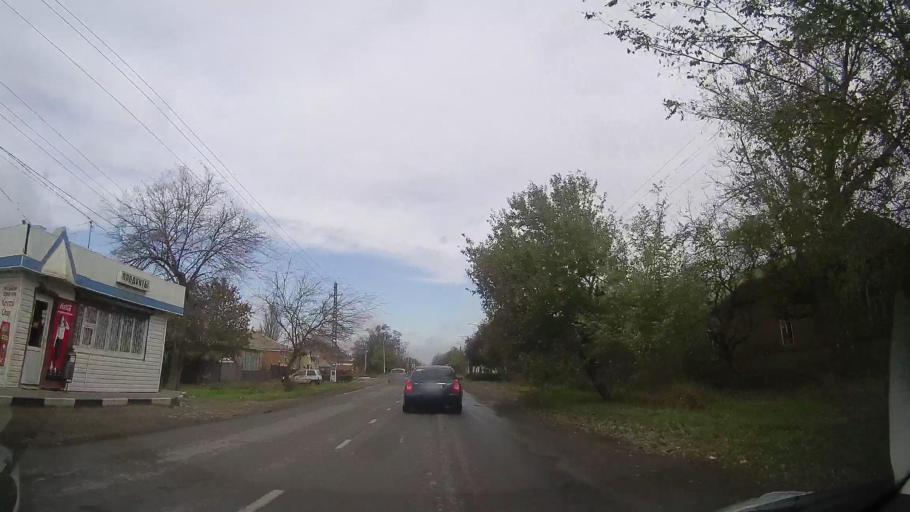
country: RU
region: Rostov
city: Bataysk
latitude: 47.1429
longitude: 39.7671
